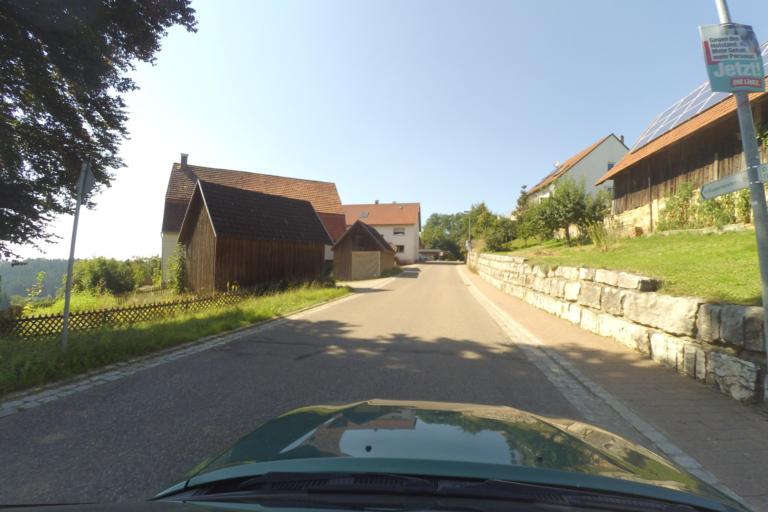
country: DE
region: Baden-Wuerttemberg
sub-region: Regierungsbezirk Stuttgart
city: Ruppertshofen
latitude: 48.8635
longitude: 9.8181
